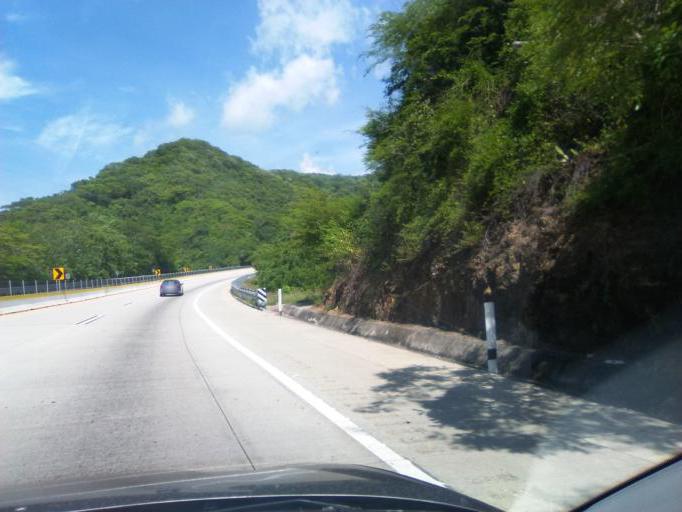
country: MX
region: Guerrero
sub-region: Acapulco de Juarez
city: Colonia Nueva Revolucion
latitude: 16.9410
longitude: -99.7818
